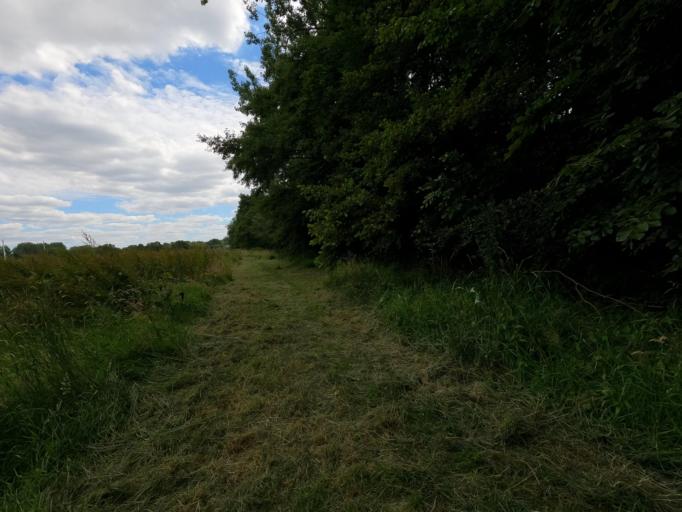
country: BE
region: Flanders
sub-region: Provincie Antwerpen
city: Edegem
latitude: 51.1478
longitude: 4.4423
